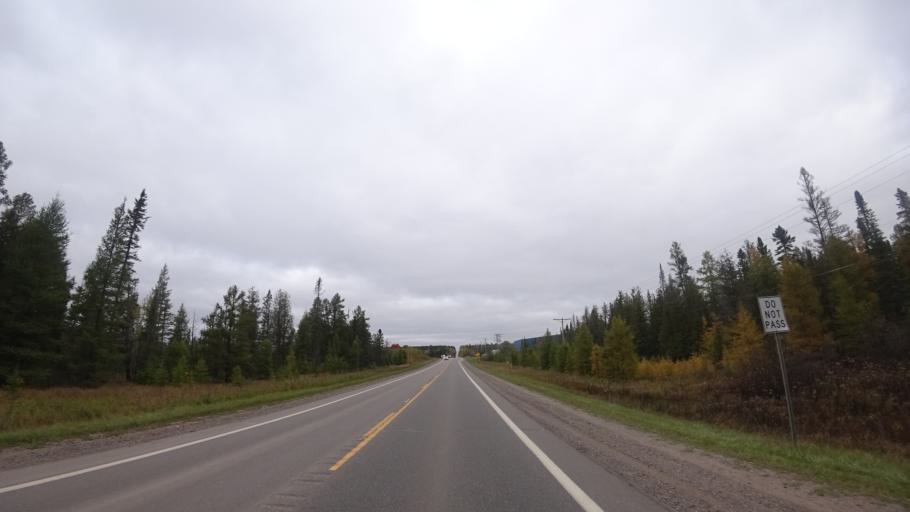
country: US
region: Wisconsin
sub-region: Florence County
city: Florence
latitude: 46.1049
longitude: -88.0758
